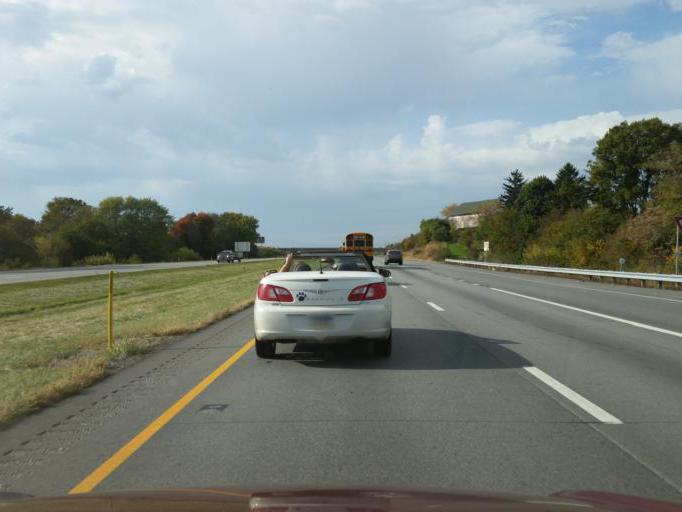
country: US
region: Pennsylvania
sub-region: Lancaster County
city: Mount Joy
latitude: 40.1258
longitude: -76.4714
